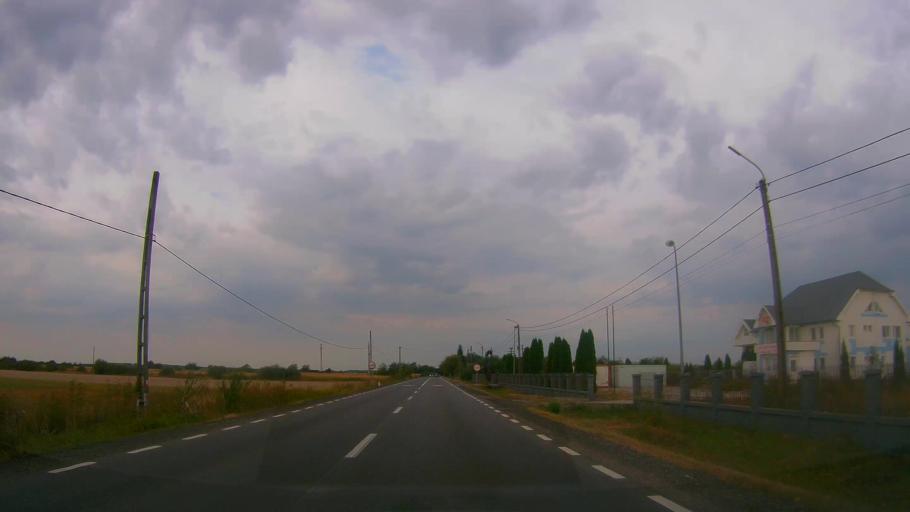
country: RO
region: Satu Mare
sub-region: Comuna Agris
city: Agris
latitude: 47.8723
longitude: 23.0368
